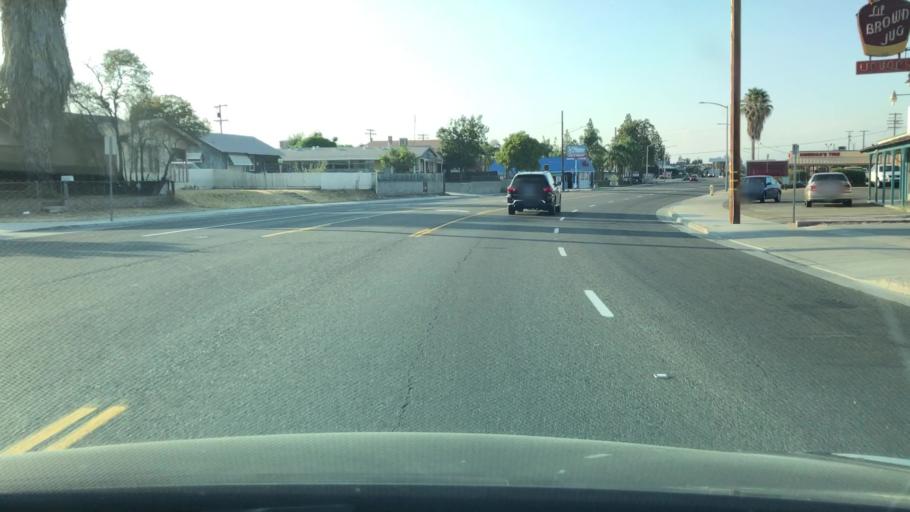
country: US
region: California
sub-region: Fresno County
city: Clovis
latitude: 36.8181
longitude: -119.7005
